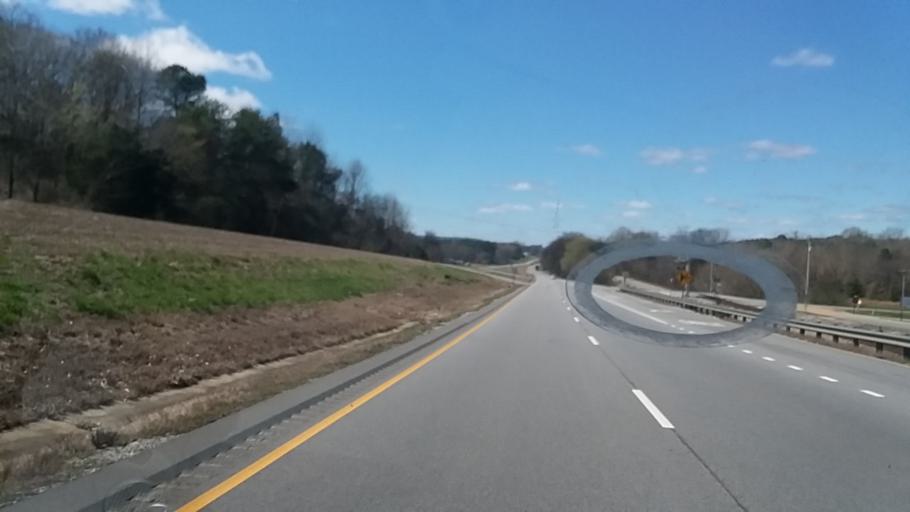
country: US
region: Alabama
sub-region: Colbert County
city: Tuscumbia
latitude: 34.7175
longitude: -87.7887
